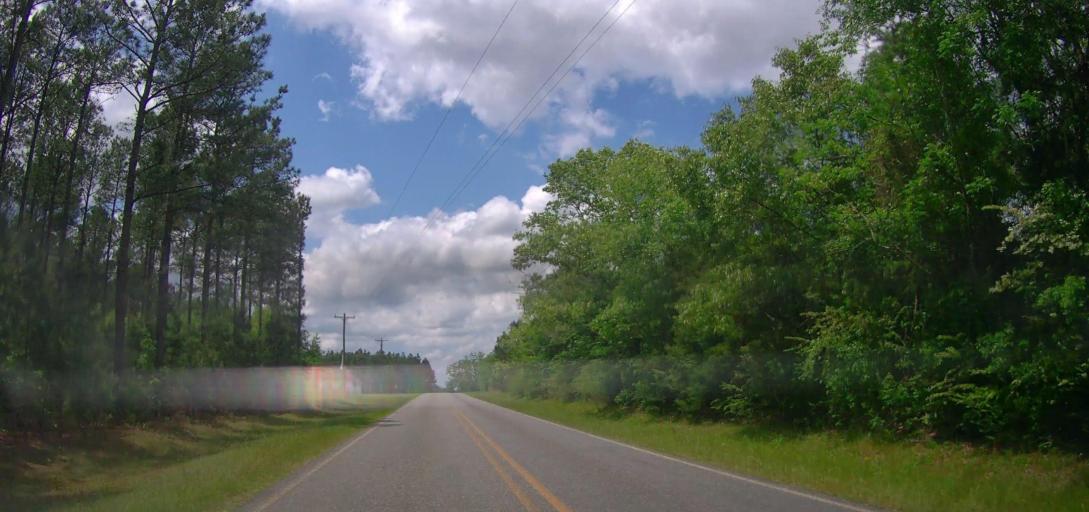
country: US
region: Georgia
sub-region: Laurens County
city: Dublin
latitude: 32.5939
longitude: -83.0224
